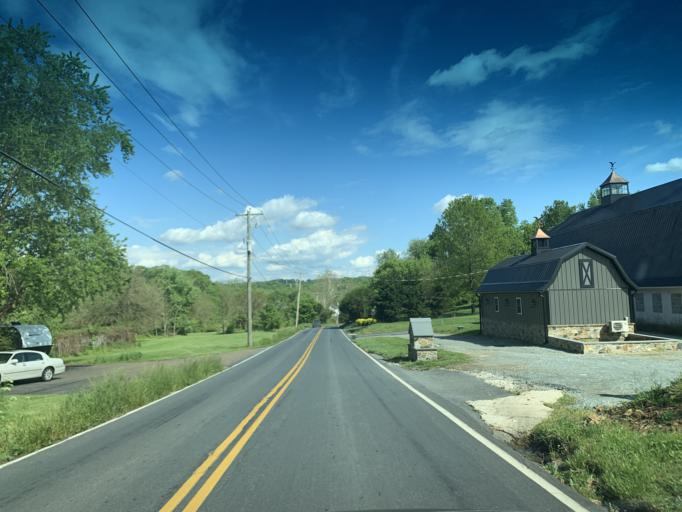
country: US
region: Maryland
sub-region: Cecil County
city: Rising Sun
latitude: 39.6927
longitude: -76.1378
